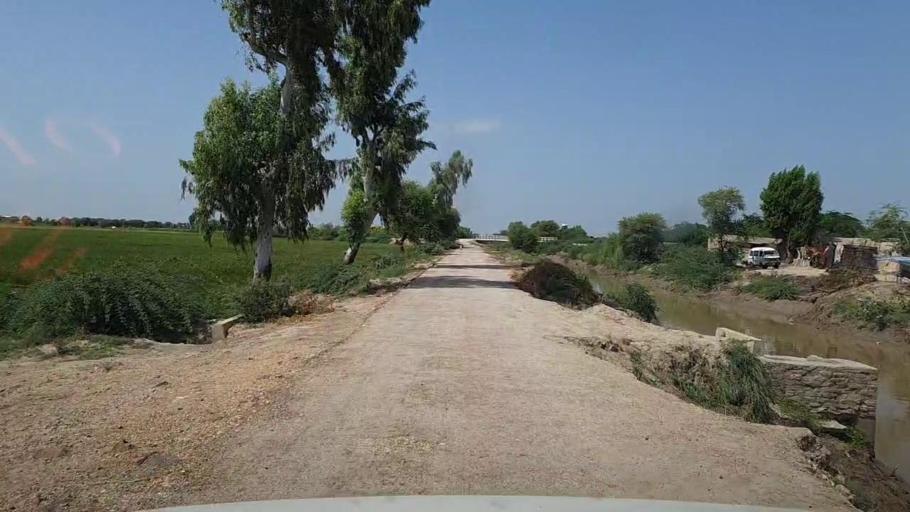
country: PK
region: Sindh
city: Kario
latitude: 24.6606
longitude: 68.5484
